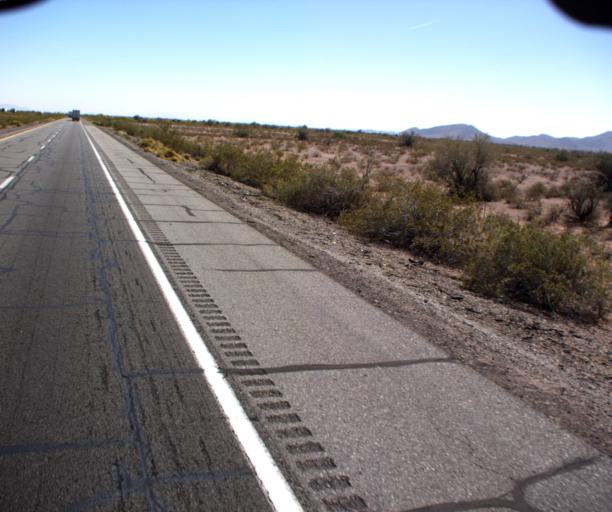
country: US
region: Arizona
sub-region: Maricopa County
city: Buckeye
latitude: 33.5099
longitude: -113.0086
